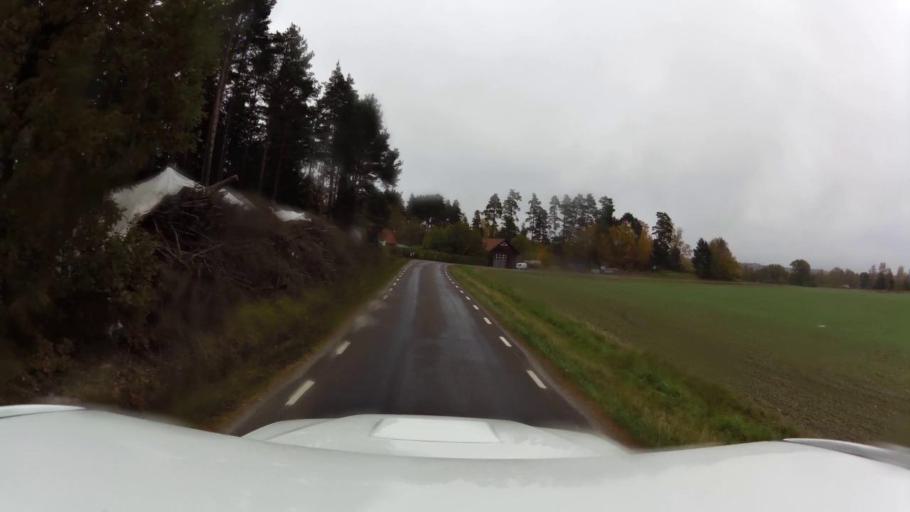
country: SE
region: OEstergoetland
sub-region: Linkopings Kommun
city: Linghem
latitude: 58.3528
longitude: 15.8693
